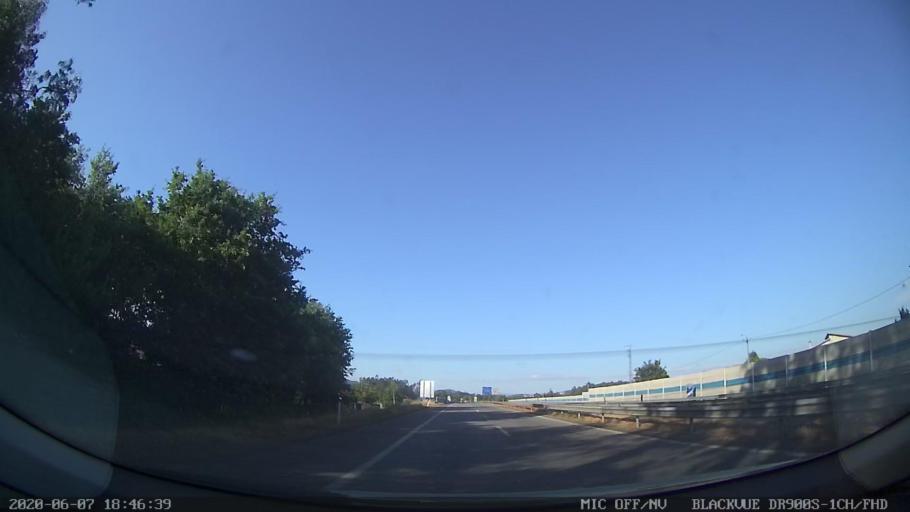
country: PT
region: Braga
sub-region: Vila Nova de Famalicao
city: Vila Nova de Famalicao
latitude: 41.3987
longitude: -8.4675
